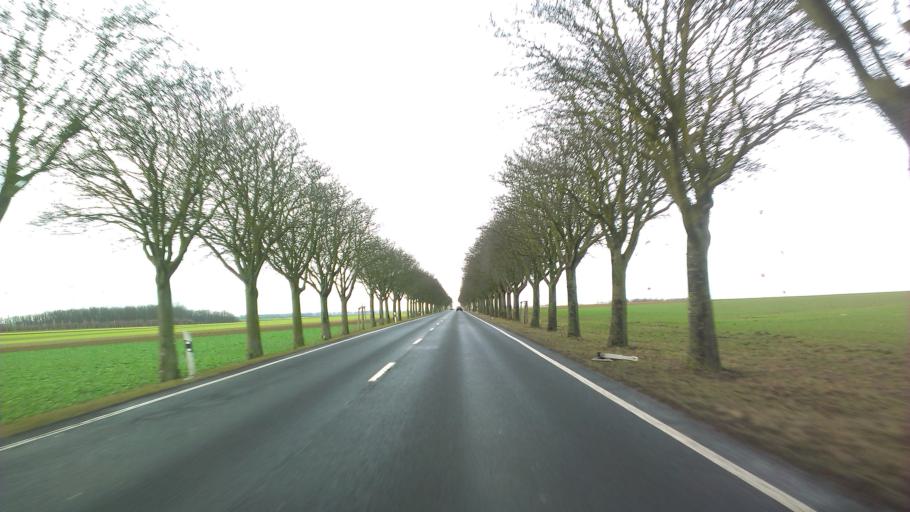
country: DE
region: Rheinland-Pfalz
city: Lonsheim
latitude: 49.7501
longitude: 8.0720
